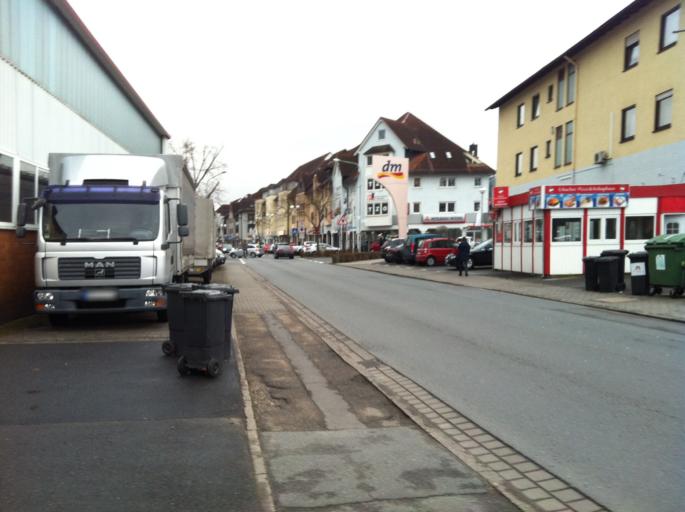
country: DE
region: Hesse
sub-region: Regierungsbezirk Darmstadt
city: Erbach
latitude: 49.6614
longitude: 8.9906
